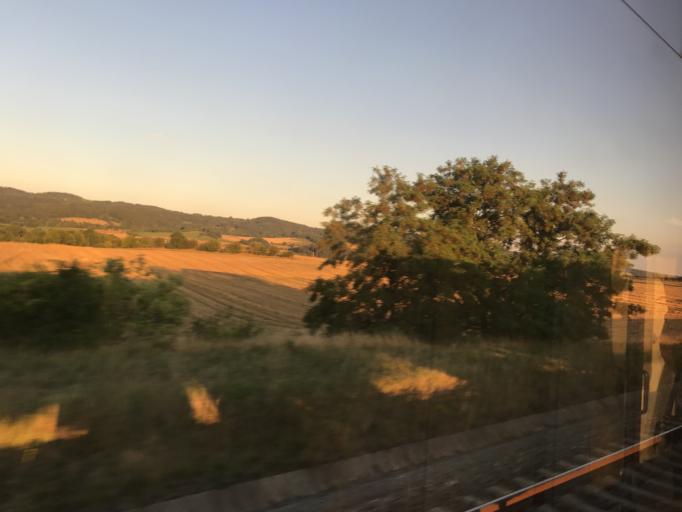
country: CZ
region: Central Bohemia
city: Votice
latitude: 49.6795
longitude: 14.6280
